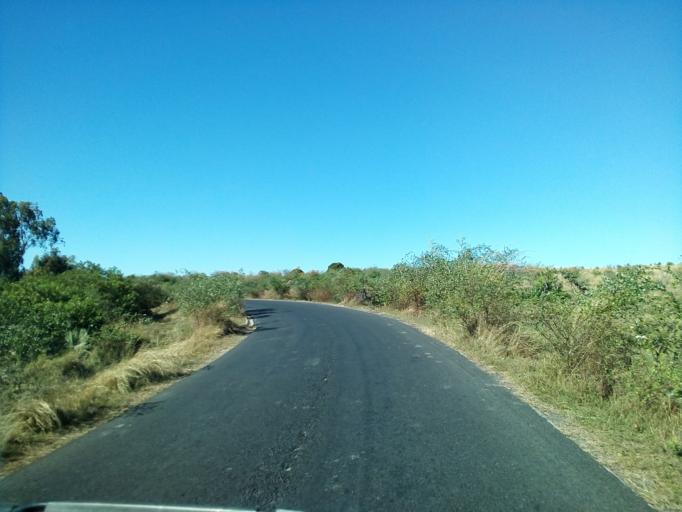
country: MG
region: Boeny
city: Marovoay
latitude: -16.0297
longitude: 46.6989
